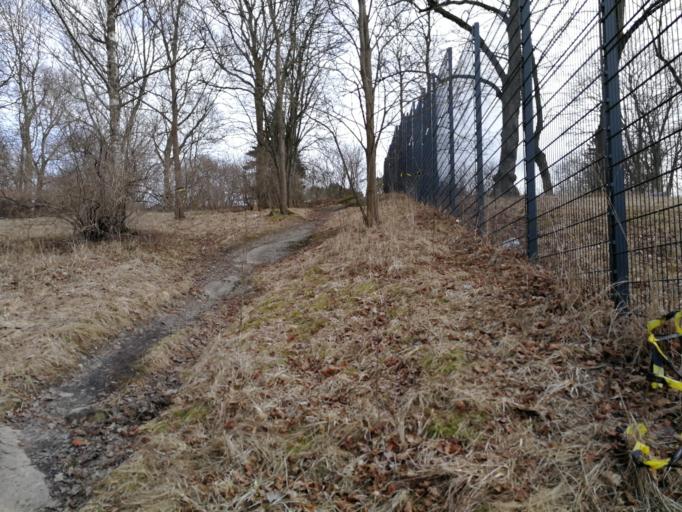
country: FI
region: Varsinais-Suomi
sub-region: Turku
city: Turku
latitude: 60.4466
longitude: 22.2666
